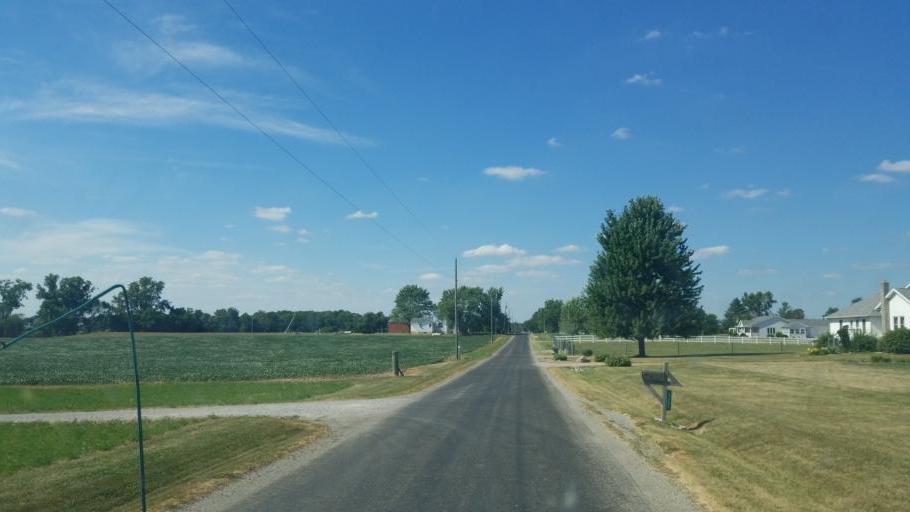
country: US
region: Ohio
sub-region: Defiance County
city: Hicksville
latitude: 41.3641
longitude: -84.7863
